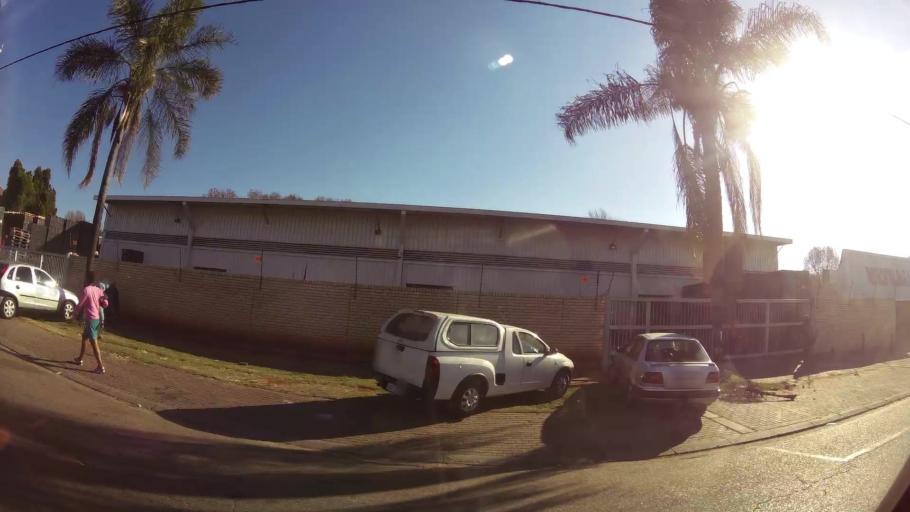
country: ZA
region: Gauteng
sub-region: City of Johannesburg Metropolitan Municipality
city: Johannesburg
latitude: -26.2026
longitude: 28.1037
